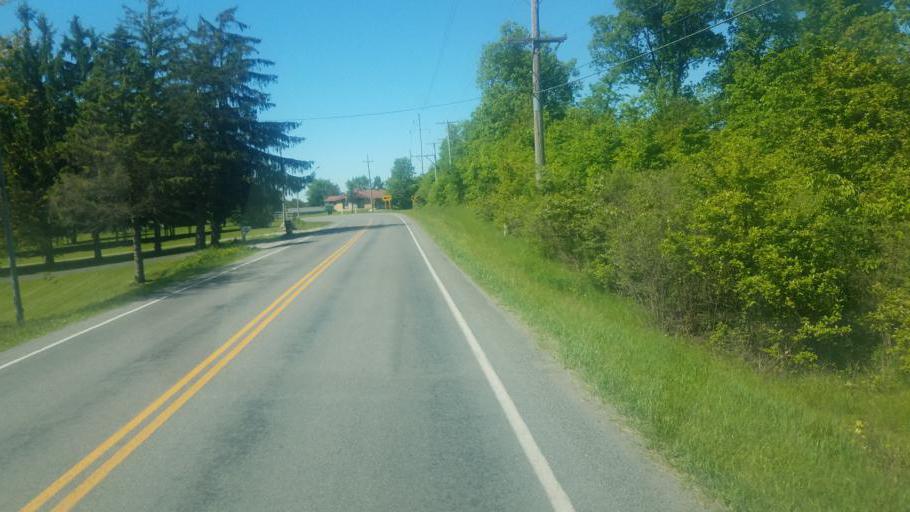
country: US
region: Ohio
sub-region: Logan County
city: Bellefontaine
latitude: 40.3792
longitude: -83.7810
